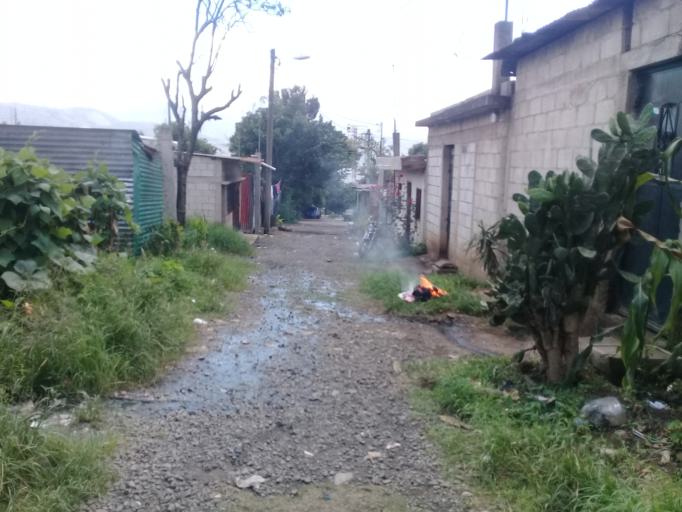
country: GT
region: Guatemala
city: Amatitlan
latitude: 14.4910
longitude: -90.6448
